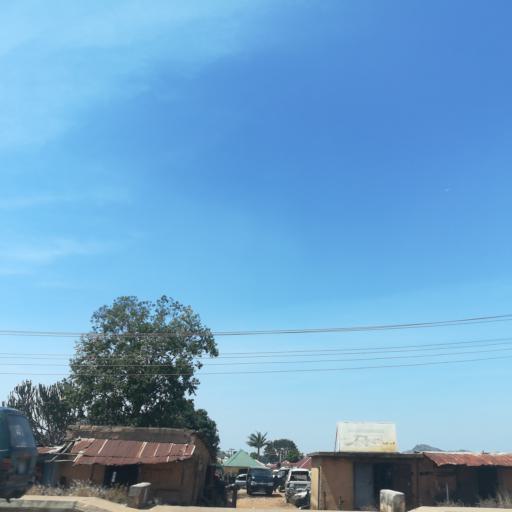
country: NG
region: Plateau
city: Bukuru
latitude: 9.8100
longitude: 8.8671
